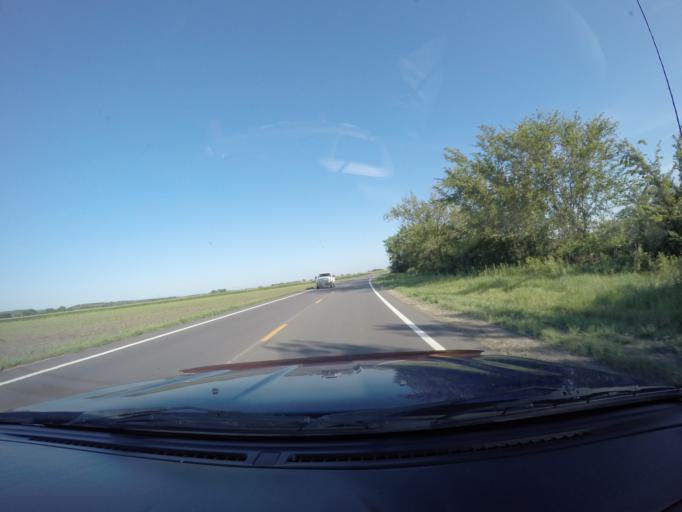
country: US
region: Kansas
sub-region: Douglas County
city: Lawrence
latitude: 39.0241
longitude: -95.2353
